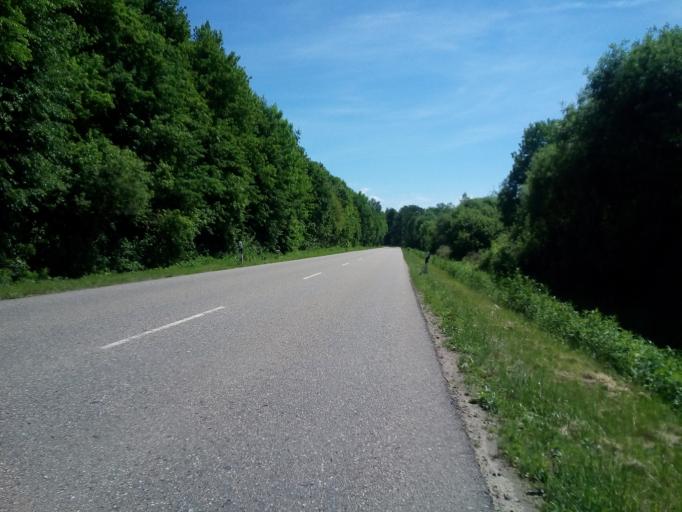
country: DE
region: Baden-Wuerttemberg
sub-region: Freiburg Region
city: Renchen
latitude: 48.6395
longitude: 7.9915
